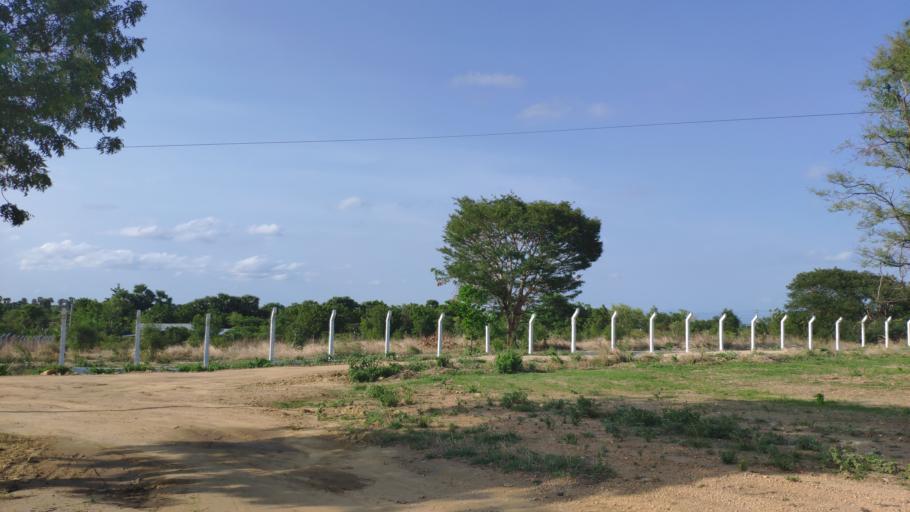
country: MM
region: Mandalay
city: Meiktila
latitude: 20.9143
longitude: 95.8603
